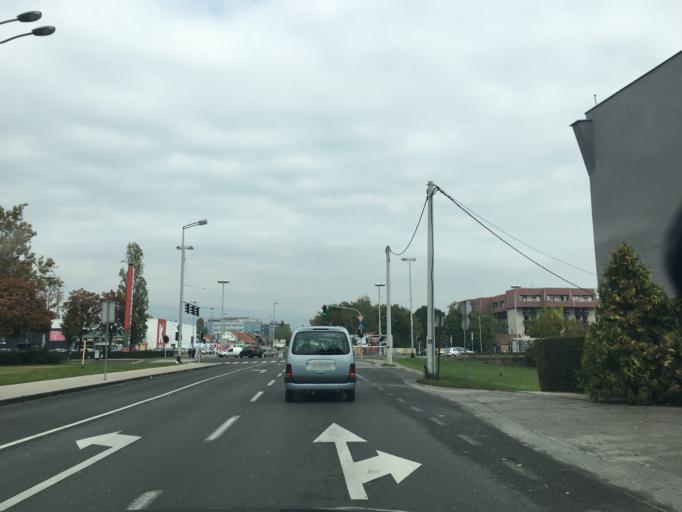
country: HR
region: Grad Zagreb
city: Novi Zagreb
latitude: 45.8023
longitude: 16.0151
